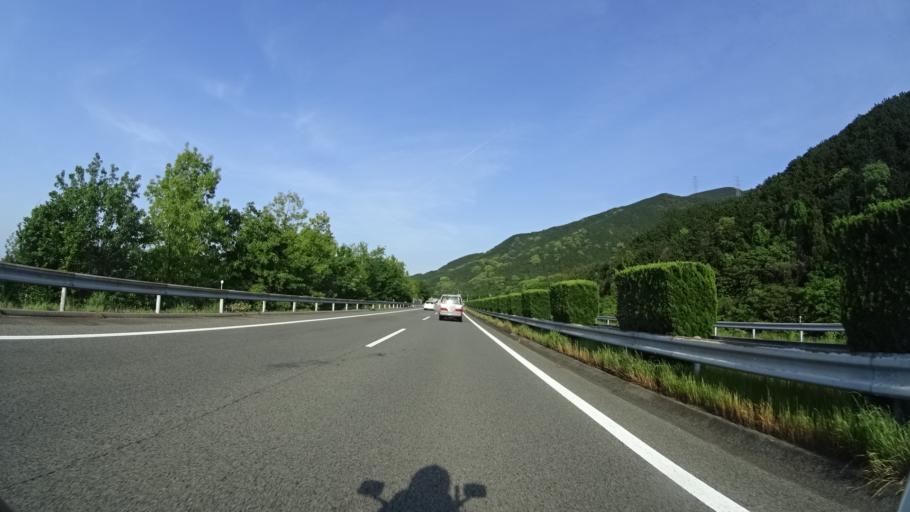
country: JP
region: Ehime
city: Kawanoecho
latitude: 33.9556
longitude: 133.4630
